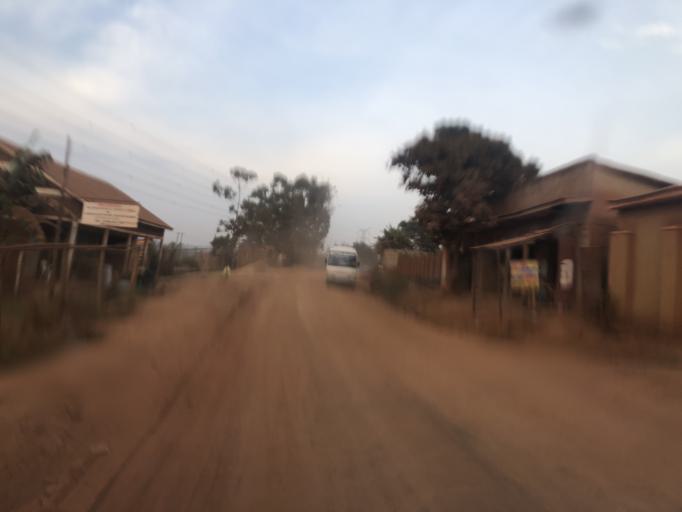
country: UG
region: Central Region
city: Kampala Central Division
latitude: 0.3001
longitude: 32.5148
